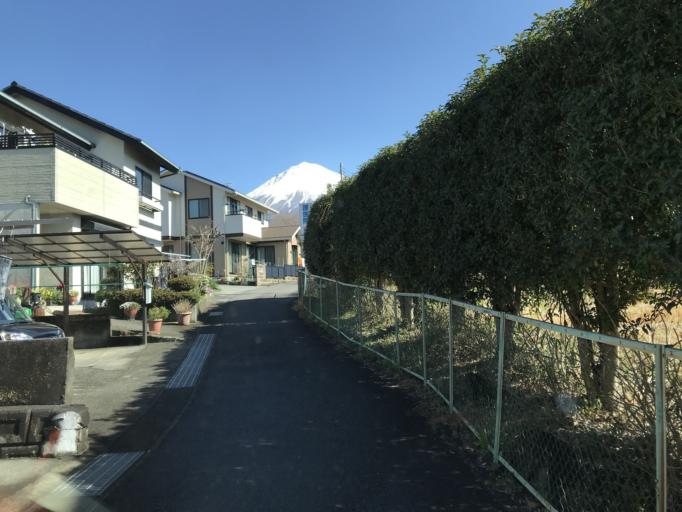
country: JP
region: Shizuoka
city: Fujinomiya
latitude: 35.2603
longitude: 138.6307
